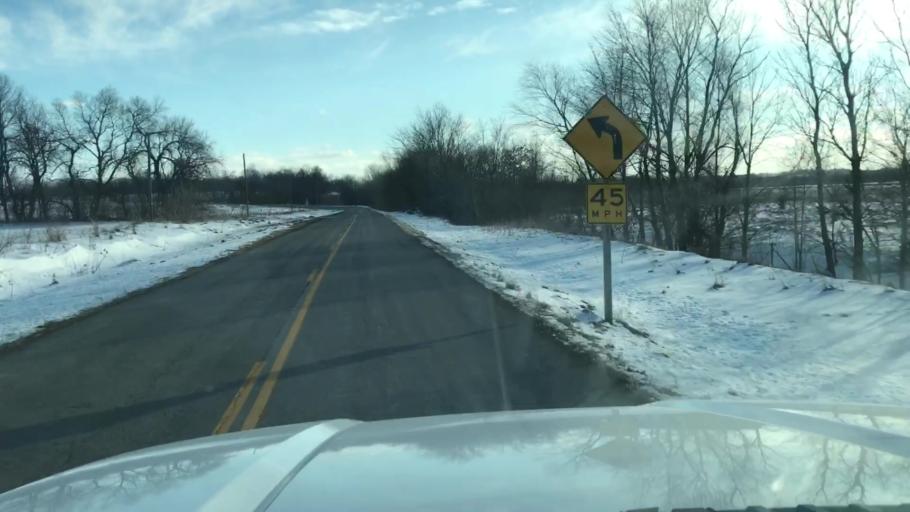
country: US
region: Missouri
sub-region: Holt County
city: Oregon
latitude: 40.1055
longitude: -95.0226
